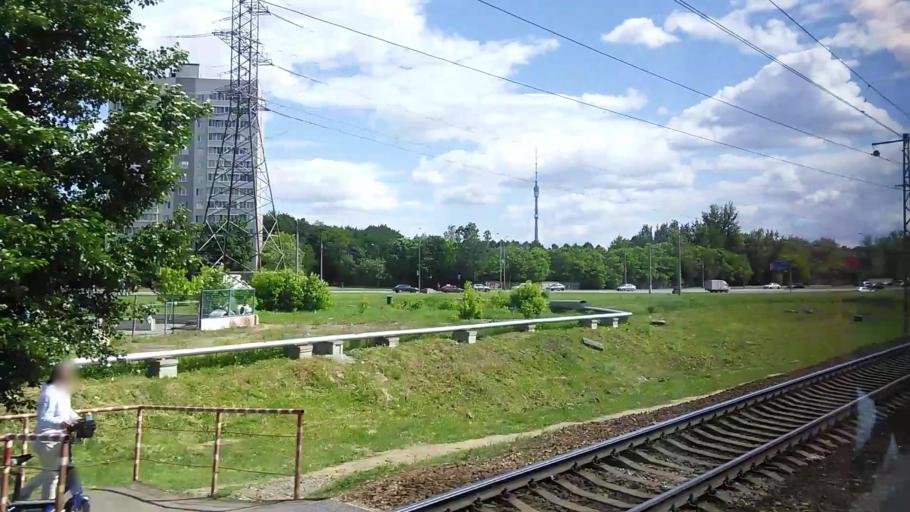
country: RU
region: Moscow
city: Novovladykino
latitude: 55.8398
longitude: 37.5789
